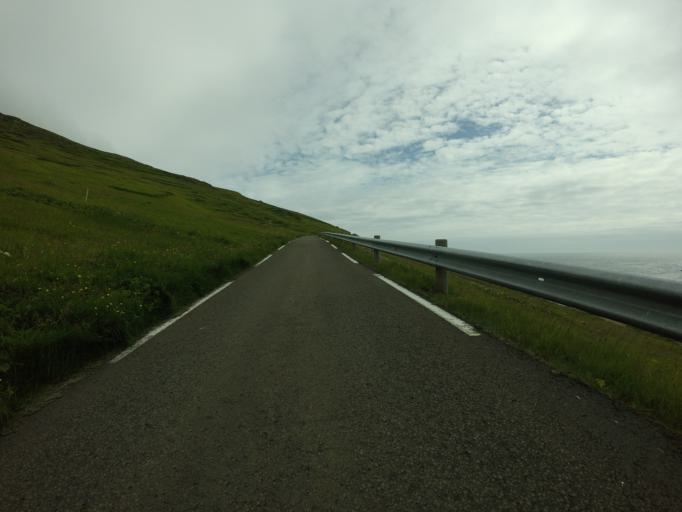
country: FO
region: Sandoy
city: Sandur
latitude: 61.7857
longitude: -6.6757
